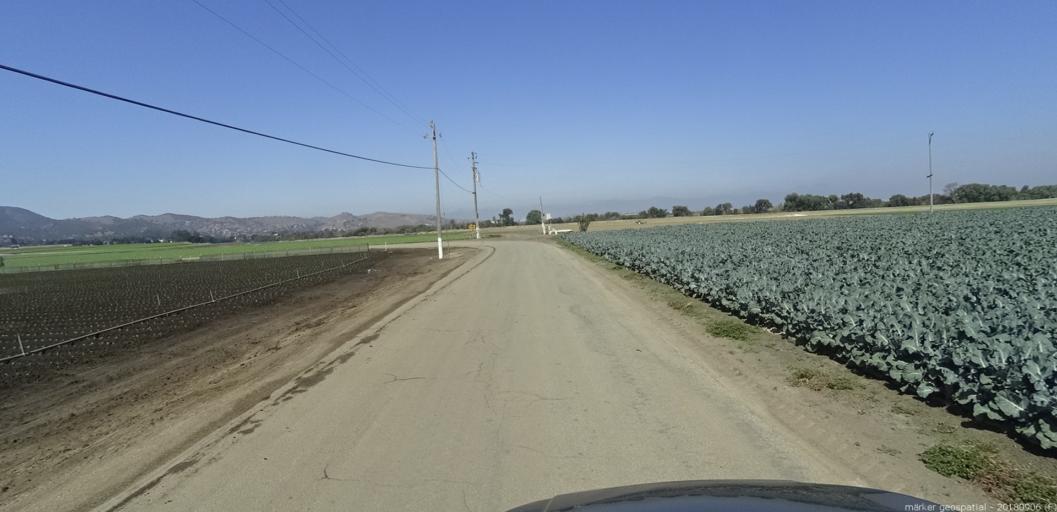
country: US
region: California
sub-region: Monterey County
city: Salinas
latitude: 36.6013
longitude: -121.6145
